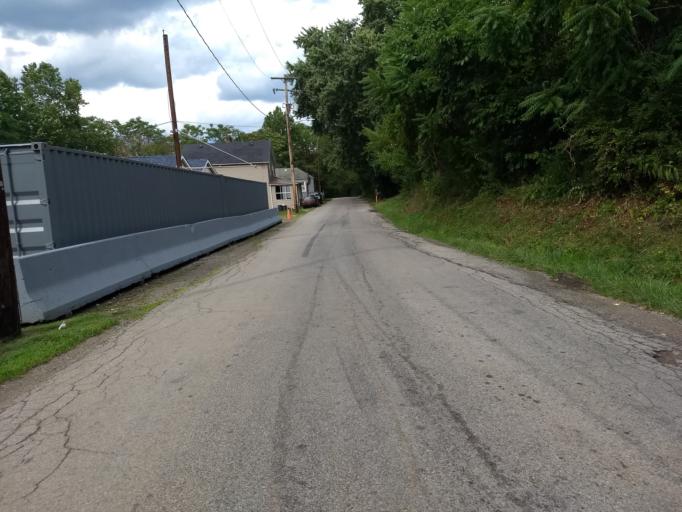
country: US
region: Pennsylvania
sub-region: Allegheny County
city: Brackenridge
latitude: 40.6121
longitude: -79.7131
